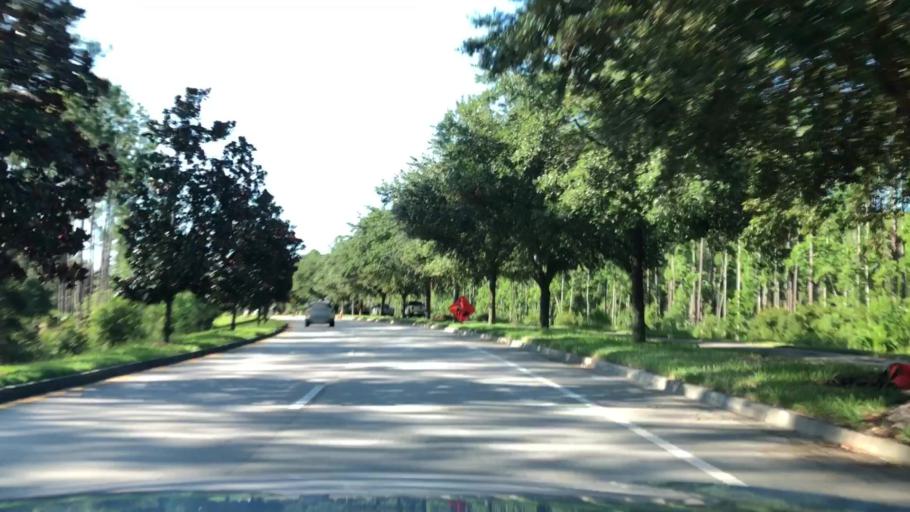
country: US
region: Florida
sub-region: Saint Johns County
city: Palm Valley
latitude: 30.0978
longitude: -81.4099
